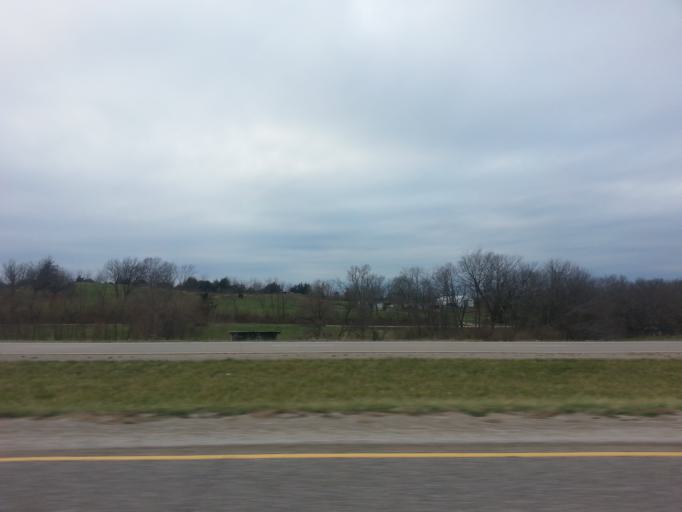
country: US
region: Iowa
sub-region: Henry County
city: Mount Pleasant
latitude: 40.9176
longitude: -91.5433
